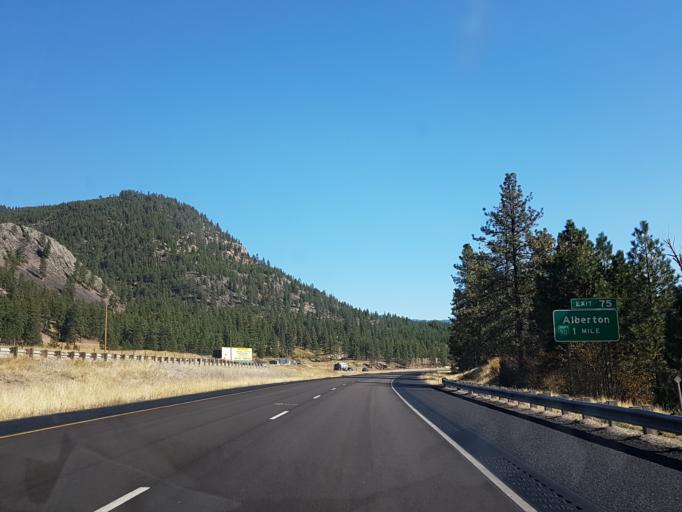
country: US
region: Montana
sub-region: Missoula County
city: Frenchtown
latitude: 47.0180
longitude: -114.5120
